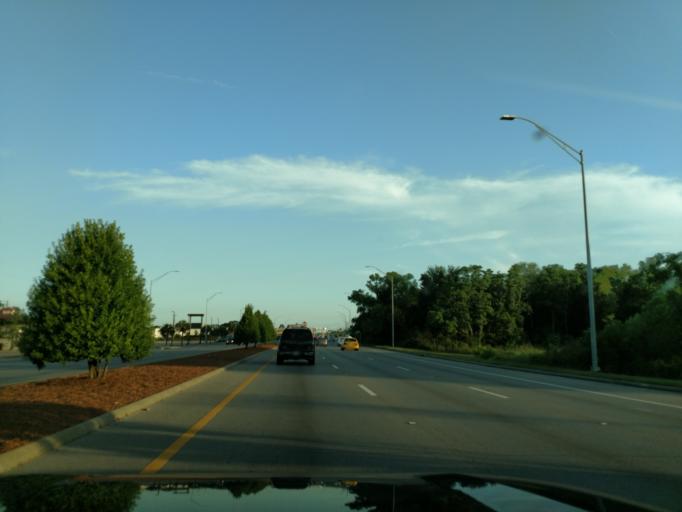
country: US
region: Mississippi
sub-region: Harrison County
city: West Gulfport
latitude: 30.4011
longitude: -89.0929
